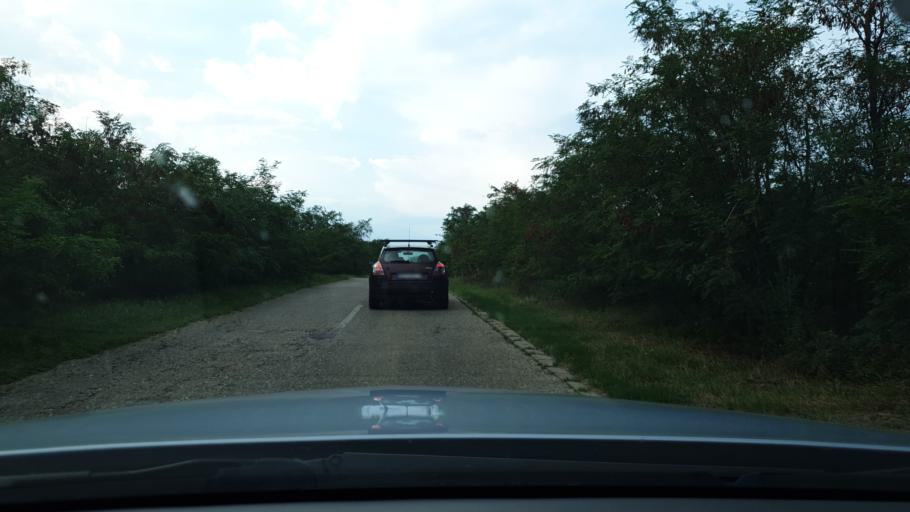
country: RS
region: Autonomna Pokrajina Vojvodina
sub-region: Juznobanatski Okrug
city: Vrsac
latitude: 45.1152
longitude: 21.3238
